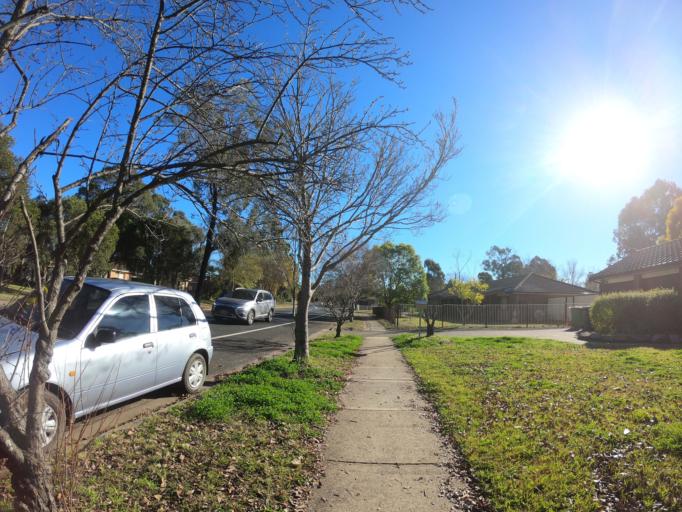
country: AU
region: New South Wales
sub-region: Hawkesbury
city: South Windsor
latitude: -33.6385
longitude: 150.7904
